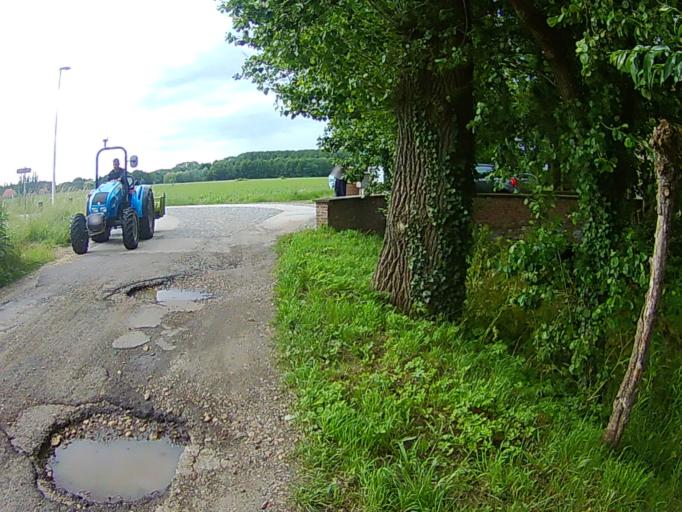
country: BE
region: Flanders
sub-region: Provincie Antwerpen
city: Ranst
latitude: 51.1633
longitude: 4.5402
